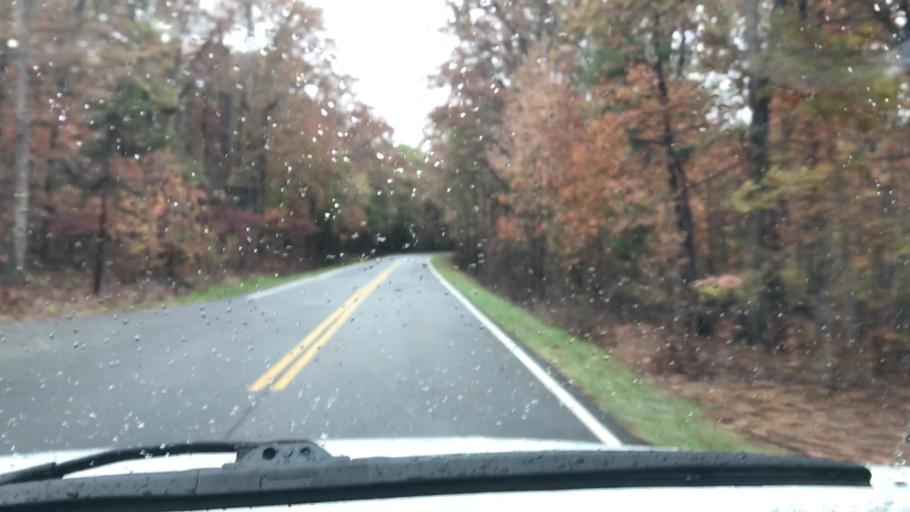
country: US
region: Virginia
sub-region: Henrico County
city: Short Pump
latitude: 37.6153
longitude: -77.6965
